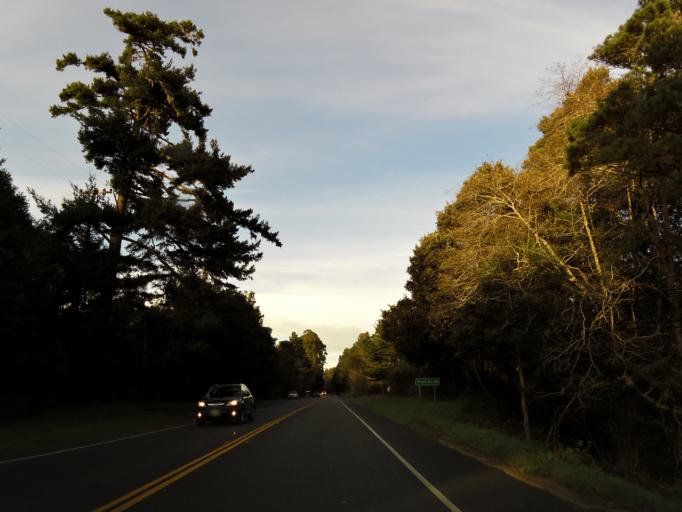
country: US
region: California
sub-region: Mendocino County
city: Fort Bragg
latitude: 39.3918
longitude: -123.8111
